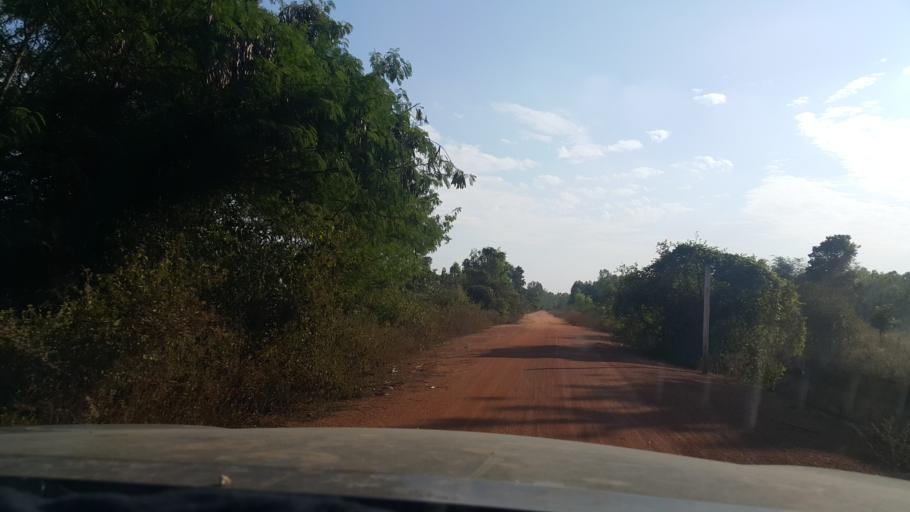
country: TH
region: Lampang
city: Hang Chat
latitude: 18.2698
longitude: 99.3720
